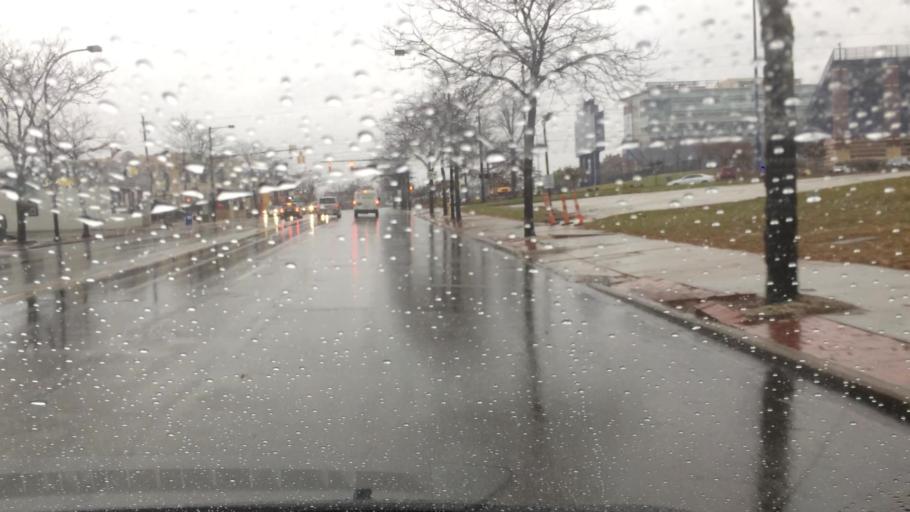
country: US
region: Ohio
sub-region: Summit County
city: Akron
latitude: 41.0712
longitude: -81.5054
